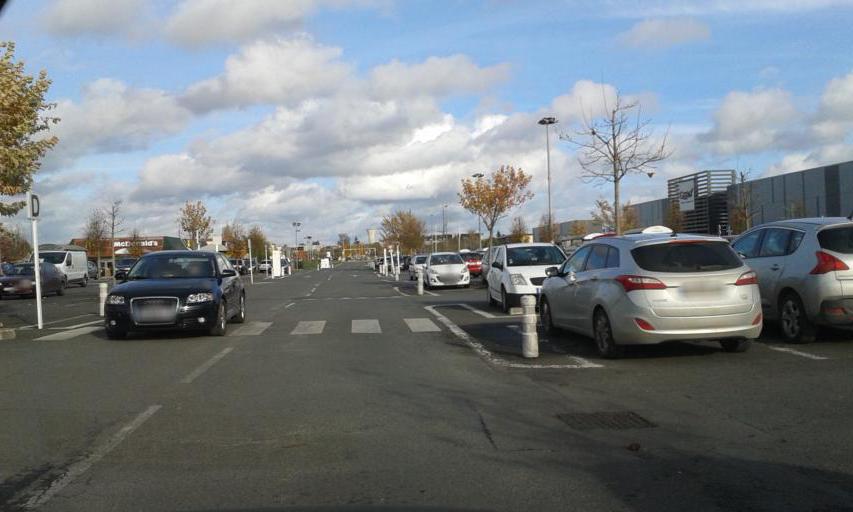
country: FR
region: Centre
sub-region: Departement du Loiret
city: Tavers
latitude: 47.7659
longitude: 1.6120
